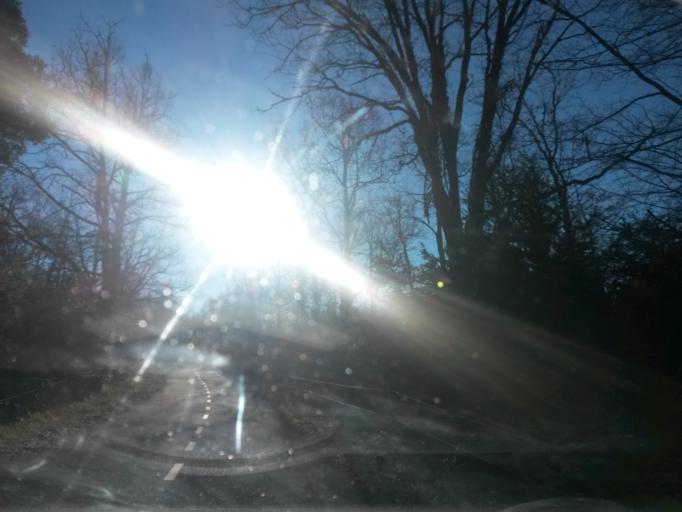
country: ES
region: Catalonia
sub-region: Provincia de Girona
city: les Planes d'Hostoles
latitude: 42.0280
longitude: 2.5313
